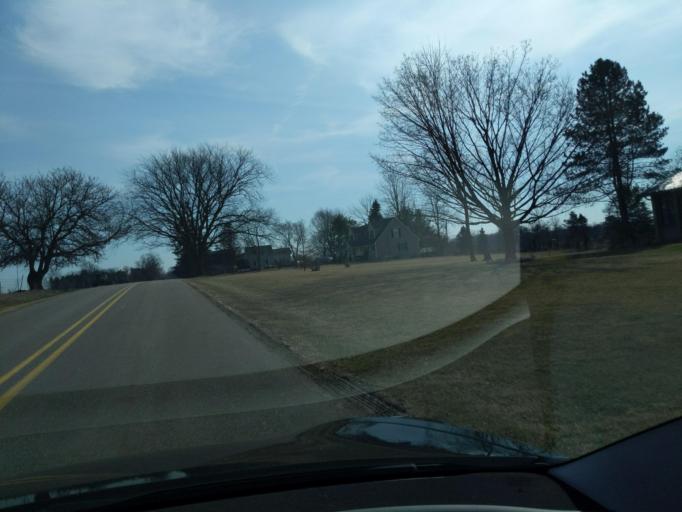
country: US
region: Michigan
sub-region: Ingham County
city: Webberville
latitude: 42.6591
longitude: -84.2186
